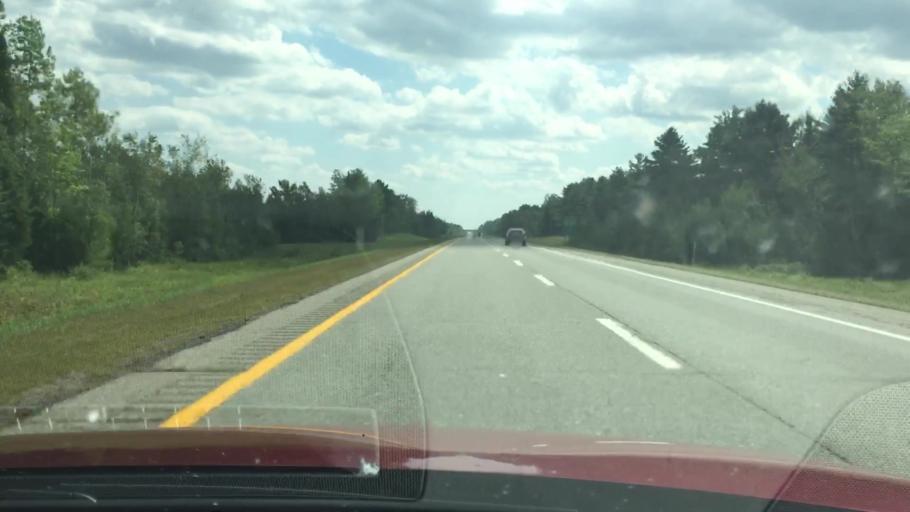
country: US
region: Maine
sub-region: Penobscot County
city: Howland
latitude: 45.2528
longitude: -68.6798
